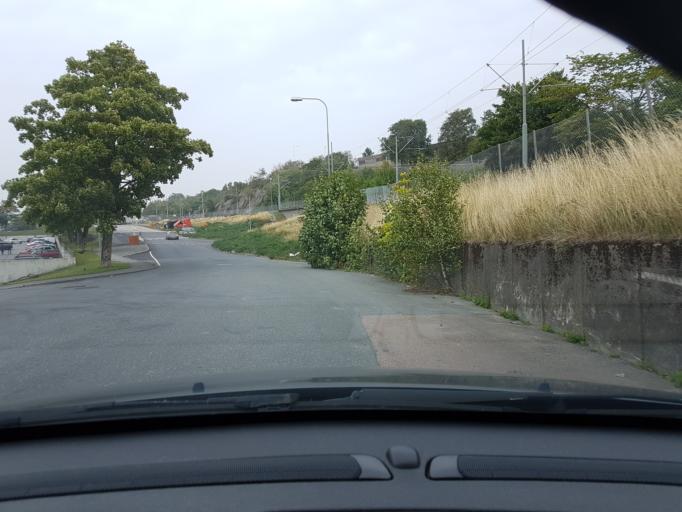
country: SE
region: Vaestra Goetaland
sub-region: Goteborg
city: Majorna
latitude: 57.6468
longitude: 11.9021
